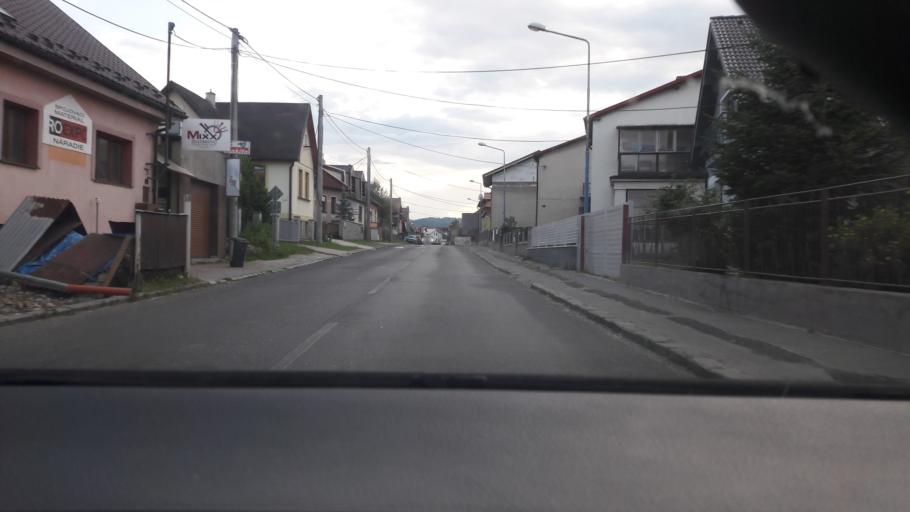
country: SK
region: Presovsky
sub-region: Okres Poprad
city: Poprad
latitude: 49.0657
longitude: 20.2761
